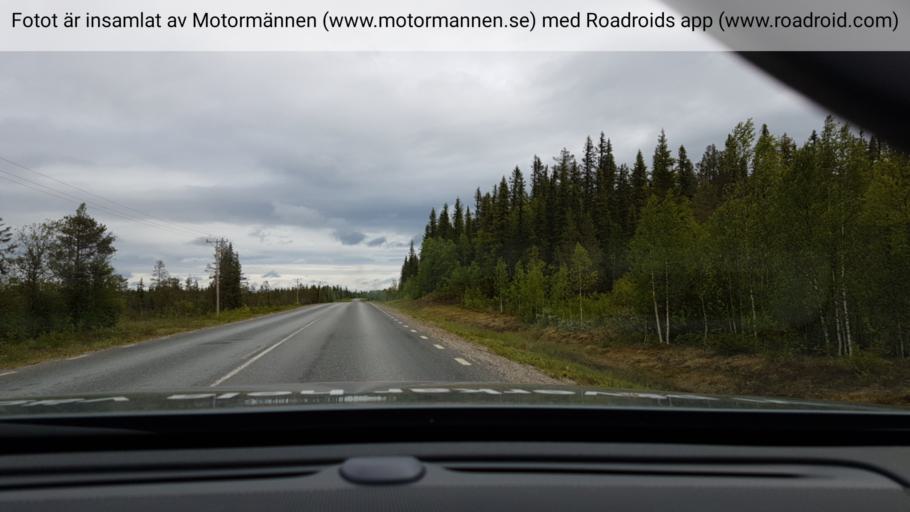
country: SE
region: Vaesterbotten
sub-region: Lycksele Kommun
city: Soderfors
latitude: 64.4108
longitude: 18.0191
